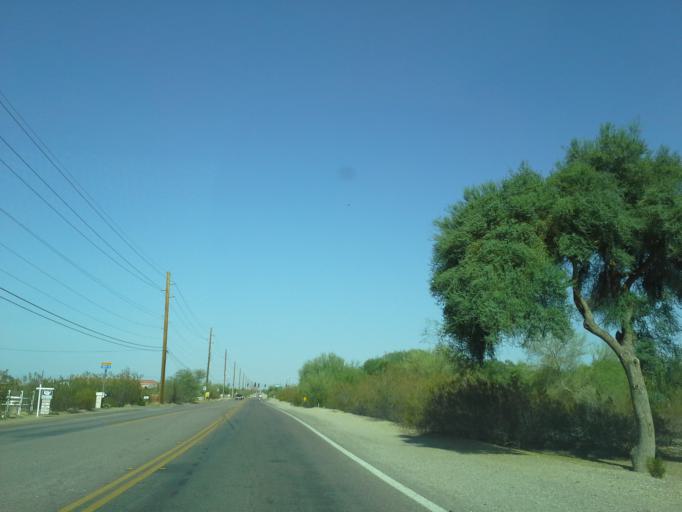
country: US
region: Arizona
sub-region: Maricopa County
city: Queen Creek
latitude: 33.2049
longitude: -111.6556
